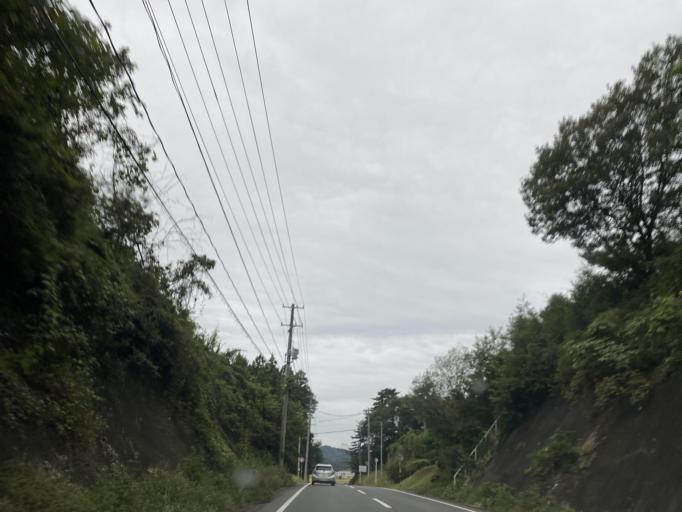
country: JP
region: Fukushima
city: Sukagawa
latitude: 37.2936
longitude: 140.2462
